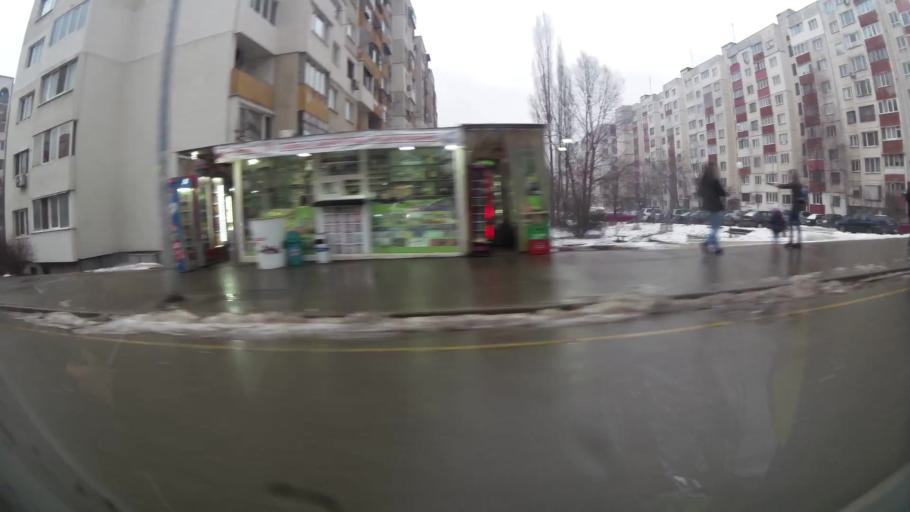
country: BG
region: Sofia-Capital
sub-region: Stolichna Obshtina
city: Sofia
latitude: 42.6870
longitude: 23.2553
